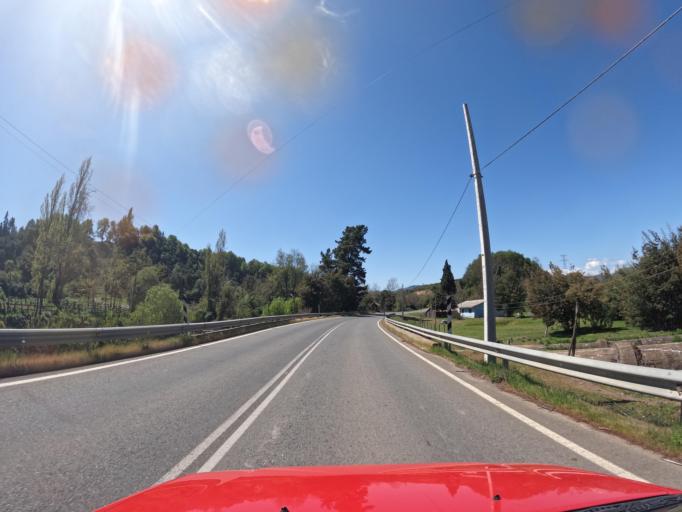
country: CL
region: Maule
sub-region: Provincia de Talca
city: San Clemente
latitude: -35.4684
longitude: -71.2749
